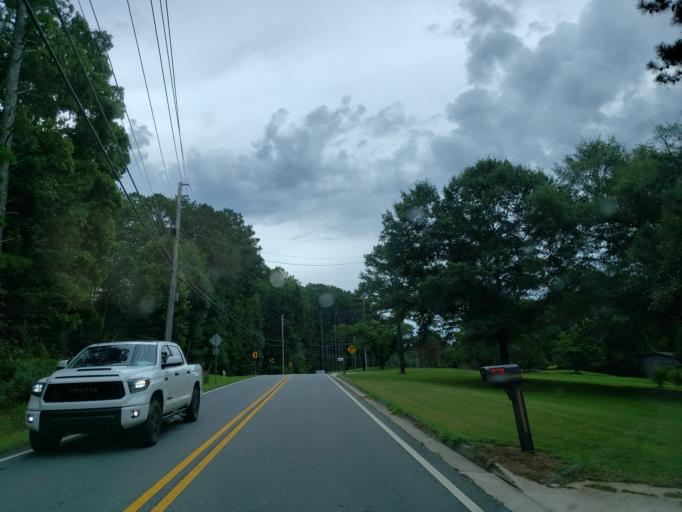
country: US
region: Georgia
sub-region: Cobb County
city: Acworth
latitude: 34.0212
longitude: -84.7058
